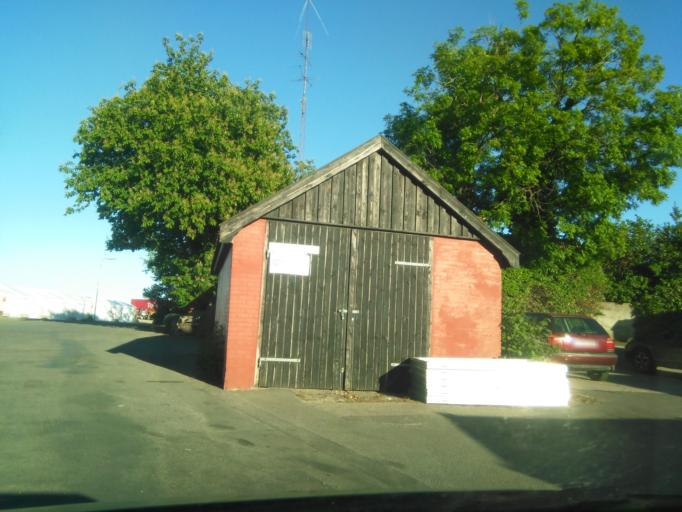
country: DK
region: Capital Region
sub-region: Bornholm Kommune
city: Ronne
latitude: 55.2772
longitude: 14.8035
